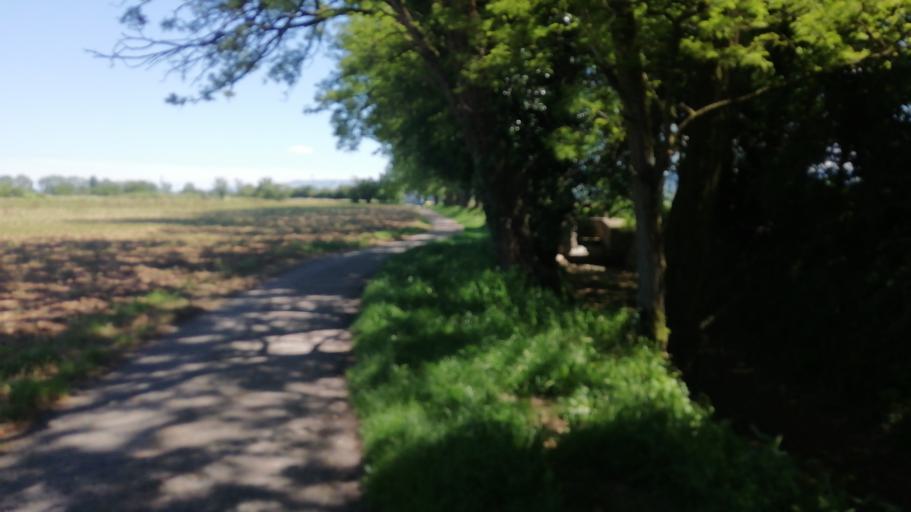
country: IT
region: Emilia-Romagna
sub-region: Provincia di Piacenza
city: Borgonovo Valtidone
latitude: 45.0038
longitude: 9.4500
